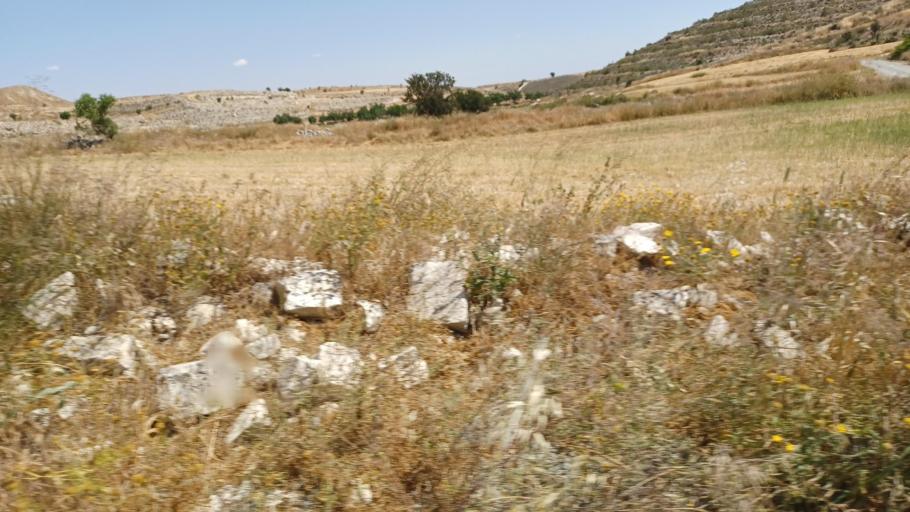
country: CY
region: Larnaka
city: Athienou
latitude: 35.0262
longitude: 33.5323
